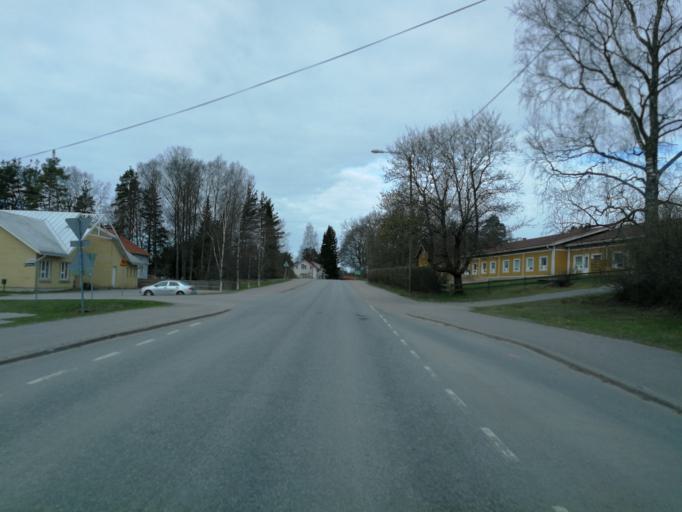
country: FI
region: Varsinais-Suomi
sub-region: Salo
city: Muurla
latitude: 60.3496
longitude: 23.2786
